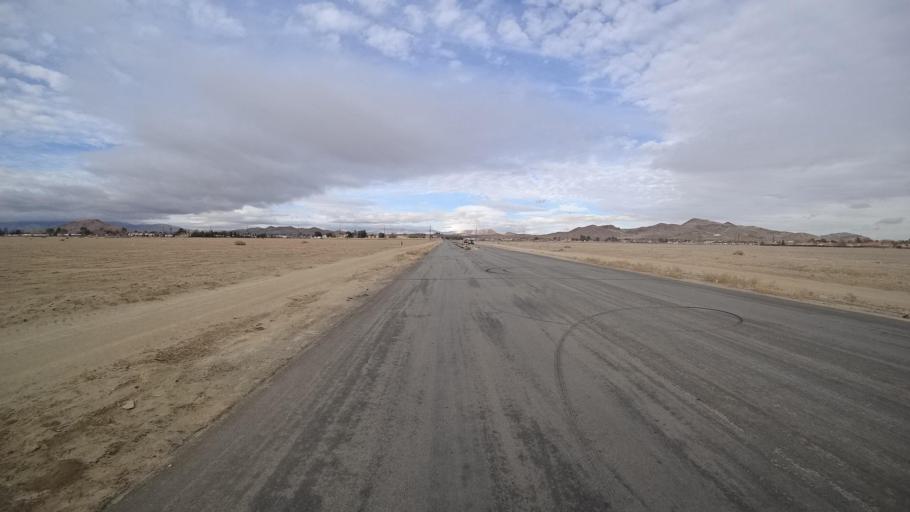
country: US
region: California
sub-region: Kern County
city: Rosamond
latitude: 34.8595
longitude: -118.2028
